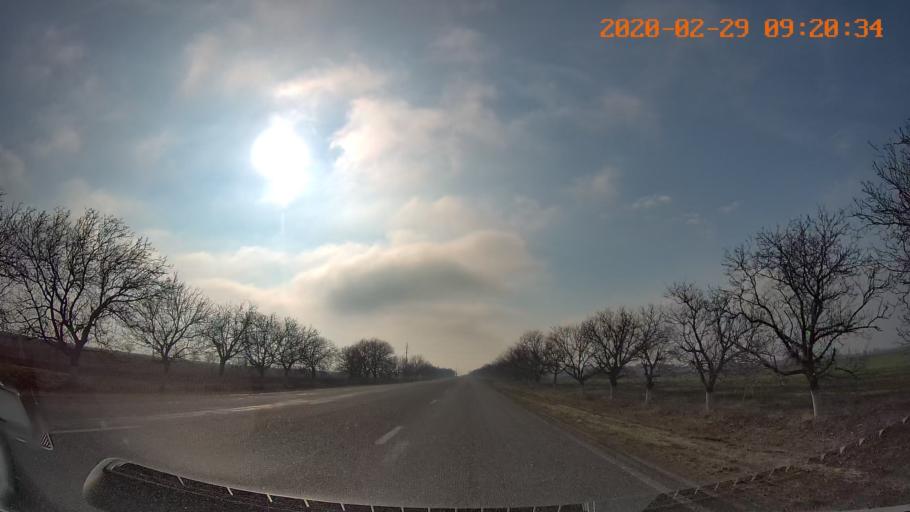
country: MD
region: Telenesti
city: Pervomaisc
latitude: 46.7472
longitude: 29.9501
